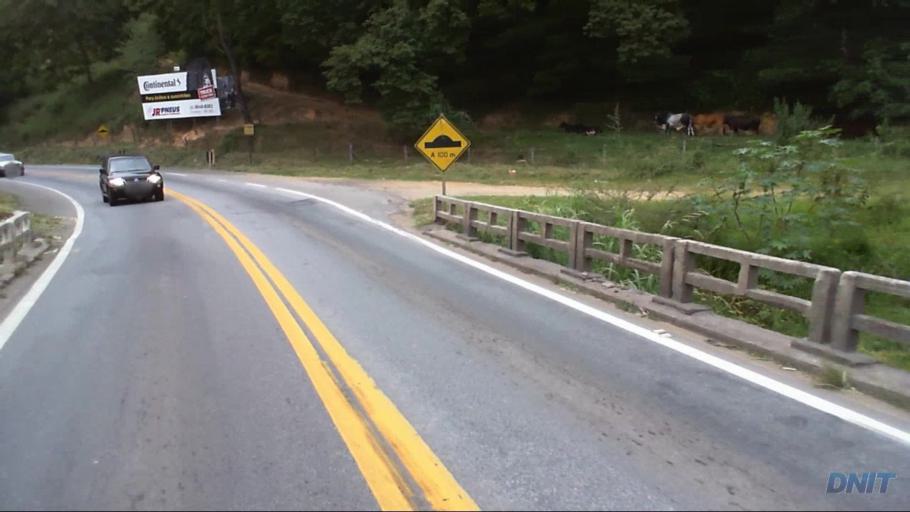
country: BR
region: Minas Gerais
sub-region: Timoteo
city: Timoteo
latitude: -19.6065
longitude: -42.7600
